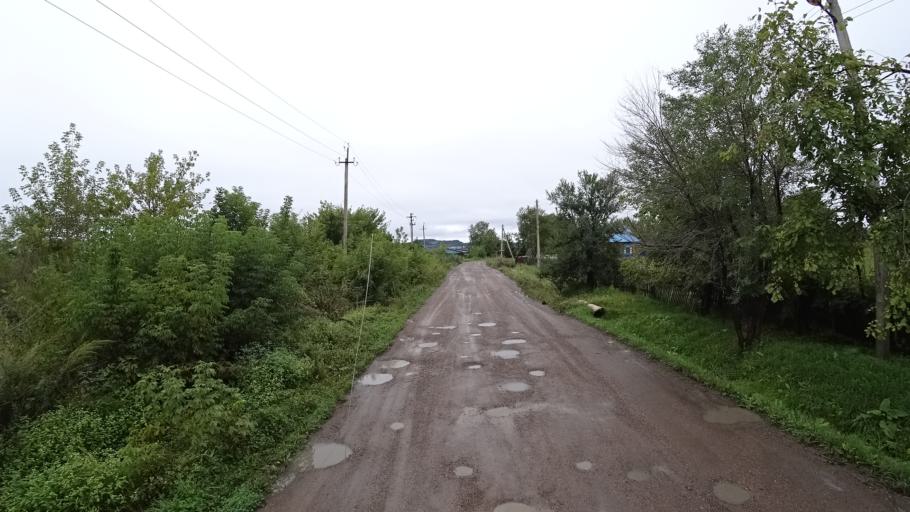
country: RU
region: Primorskiy
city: Monastyrishche
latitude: 44.1970
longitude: 132.4615
